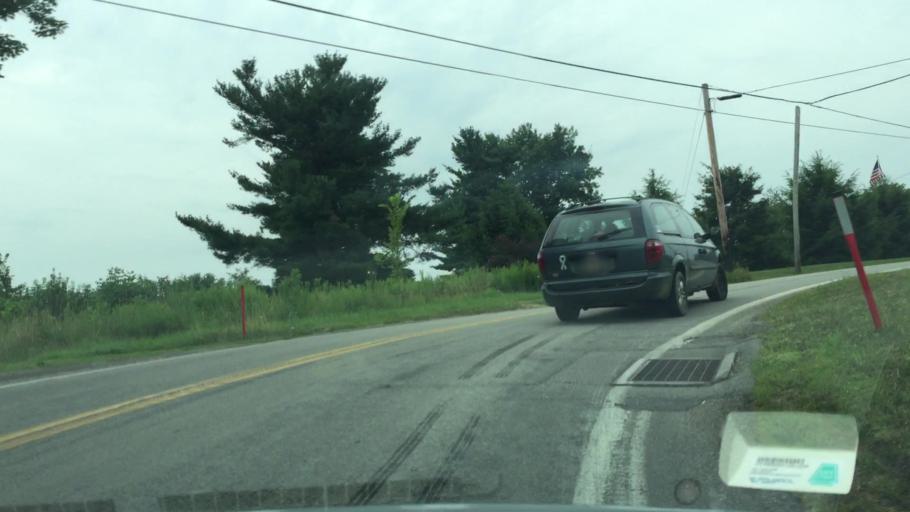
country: US
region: Pennsylvania
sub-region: Allegheny County
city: Curtisville
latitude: 40.6463
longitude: -79.8469
